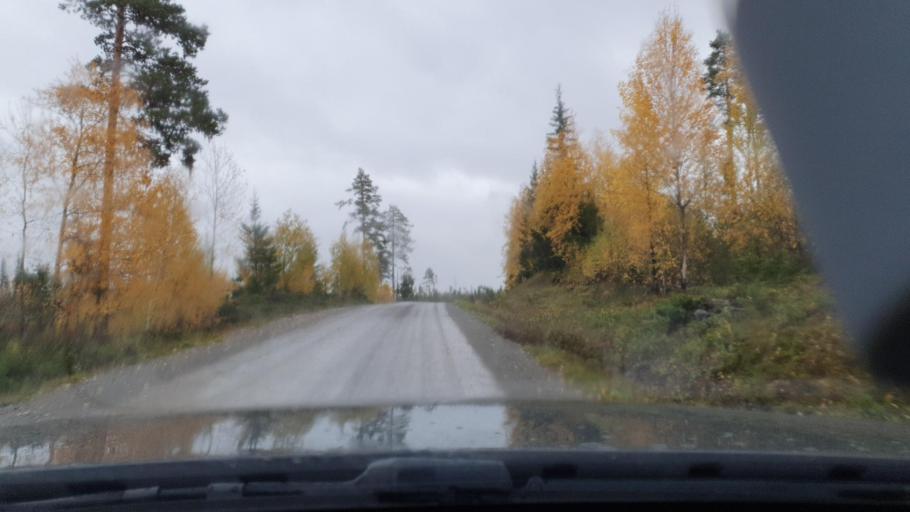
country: SE
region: Jaemtland
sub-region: Stroemsunds Kommun
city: Stroemsund
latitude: 63.5547
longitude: 15.5466
